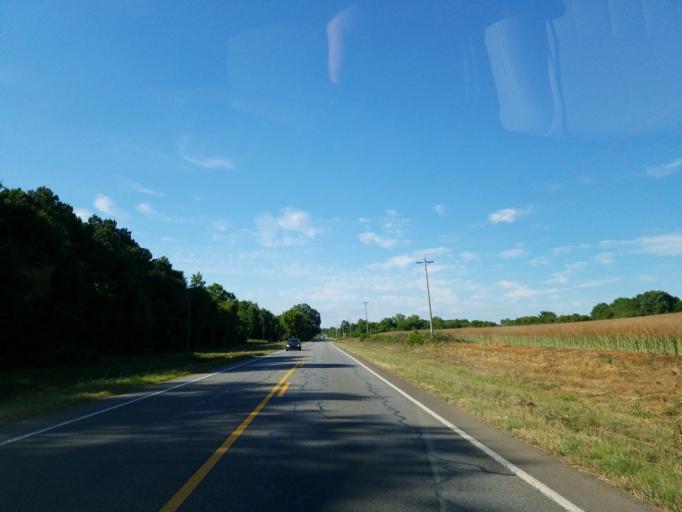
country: US
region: Georgia
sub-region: Bartow County
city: Adairsville
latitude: 34.4148
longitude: -84.9361
